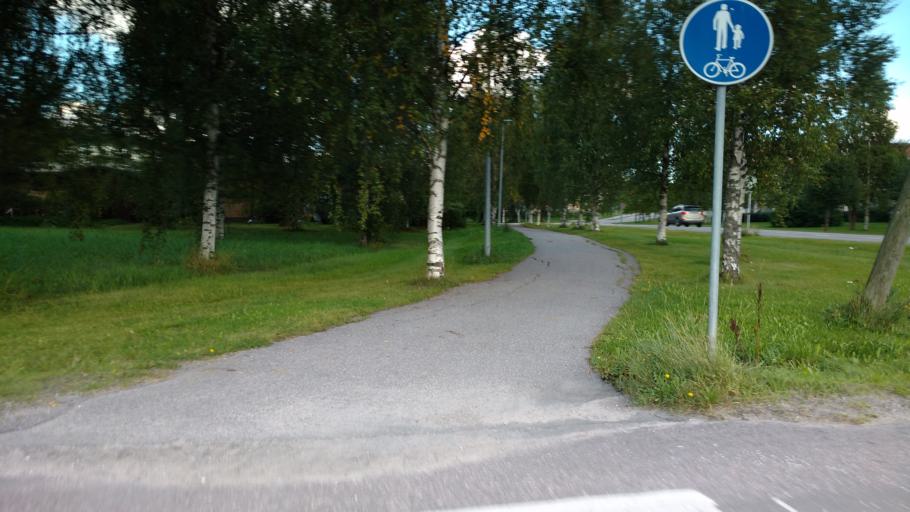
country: FI
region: Varsinais-Suomi
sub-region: Salo
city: Salo
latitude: 60.3804
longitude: 23.1503
